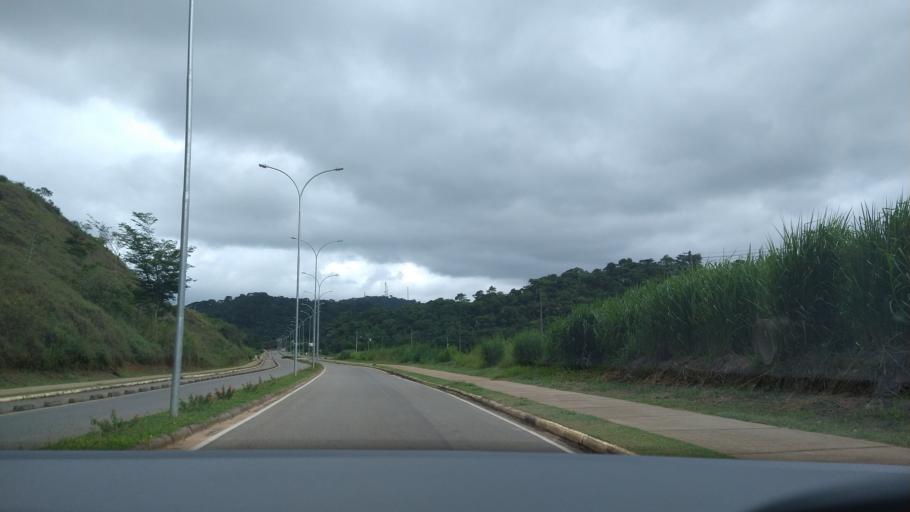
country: BR
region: Minas Gerais
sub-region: Vicosa
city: Vicosa
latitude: -20.7736
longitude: -42.8557
